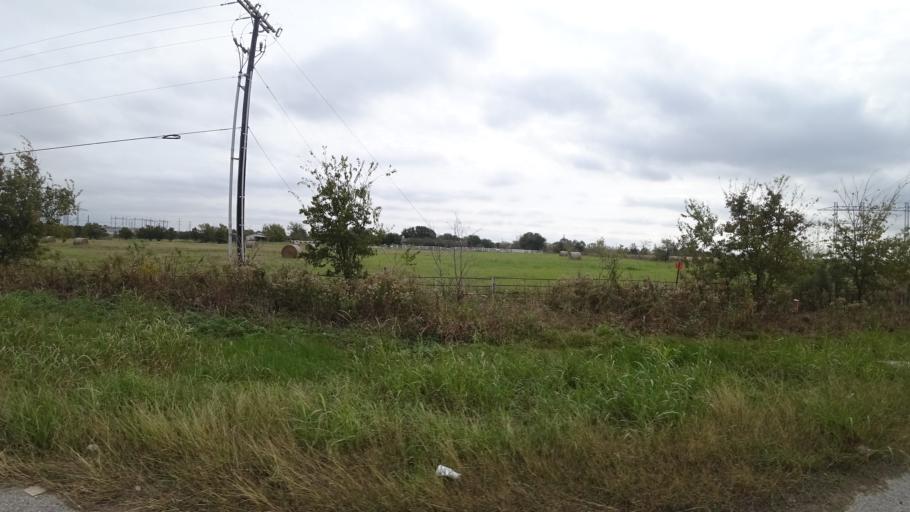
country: US
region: Texas
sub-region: Travis County
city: Pflugerville
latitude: 30.4076
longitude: -97.5820
